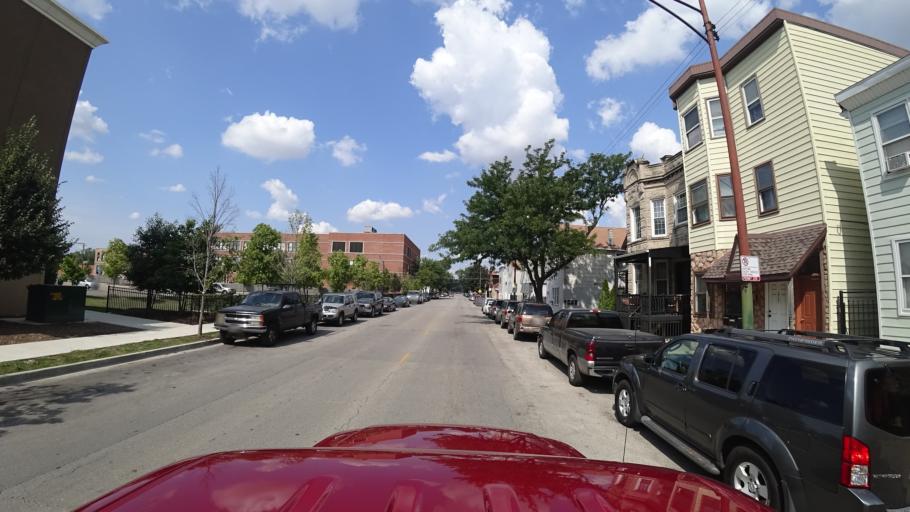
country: US
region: Illinois
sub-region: Cook County
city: Chicago
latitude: 41.8247
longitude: -87.6906
